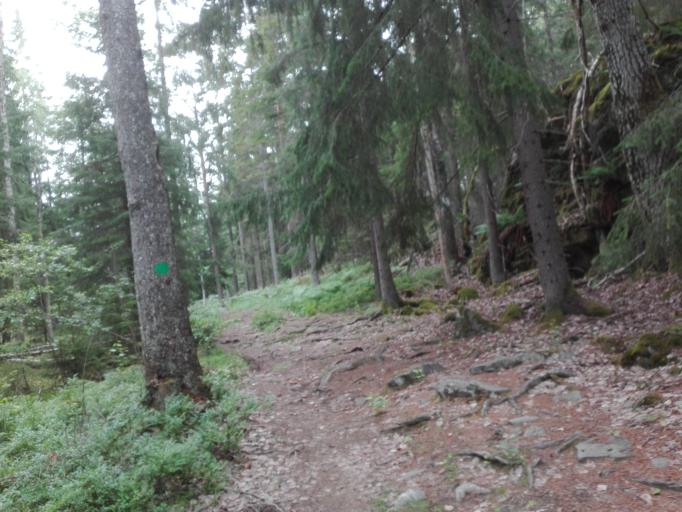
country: SE
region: Stockholm
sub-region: Nacka Kommun
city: Fisksatra
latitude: 59.2810
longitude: 18.2510
